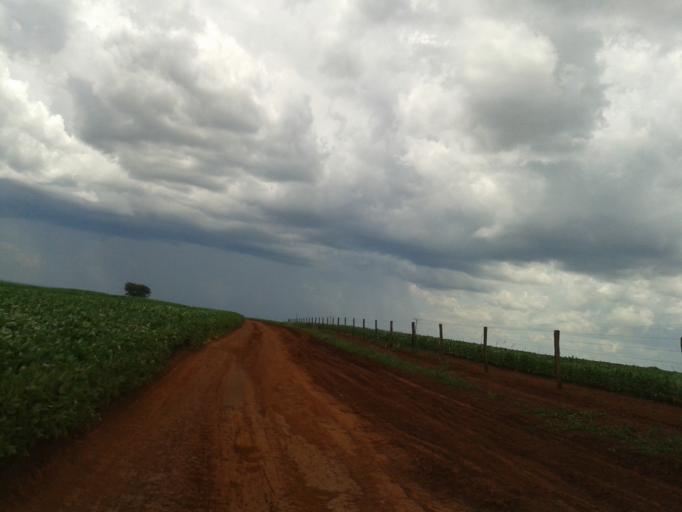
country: BR
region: Minas Gerais
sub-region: Centralina
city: Centralina
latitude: -18.7021
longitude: -49.2169
